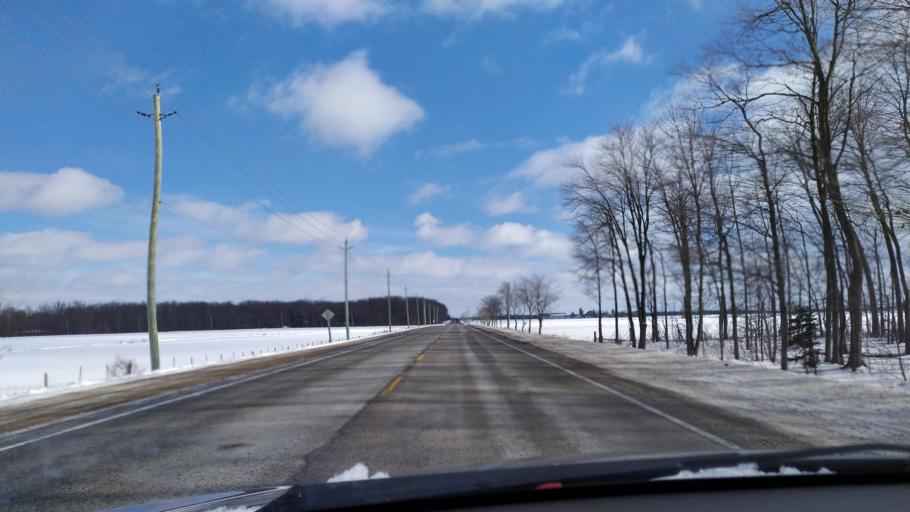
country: CA
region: Ontario
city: Waterloo
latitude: 43.5793
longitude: -80.5963
